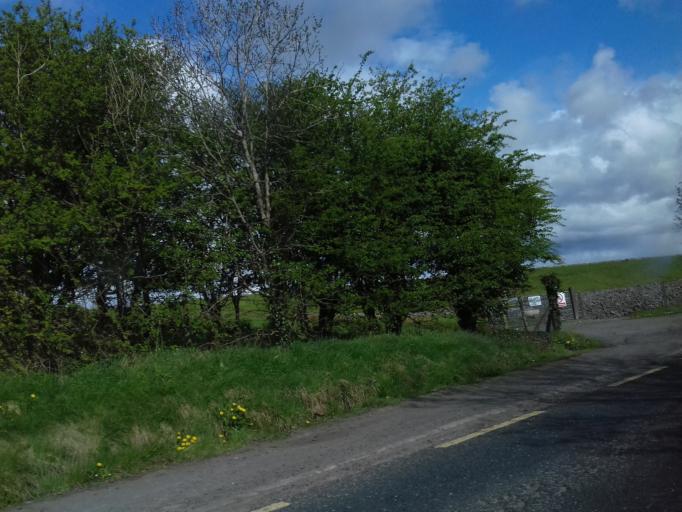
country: IE
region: Ulster
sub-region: County Donegal
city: Ballyshannon
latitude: 54.4949
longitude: -8.1699
